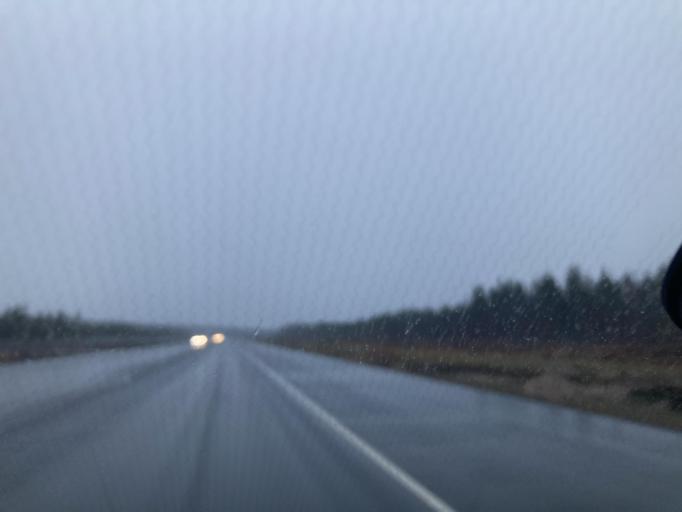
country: FI
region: Lapland
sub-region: Rovaniemi
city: Rovaniemi
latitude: 66.5681
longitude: 25.7969
